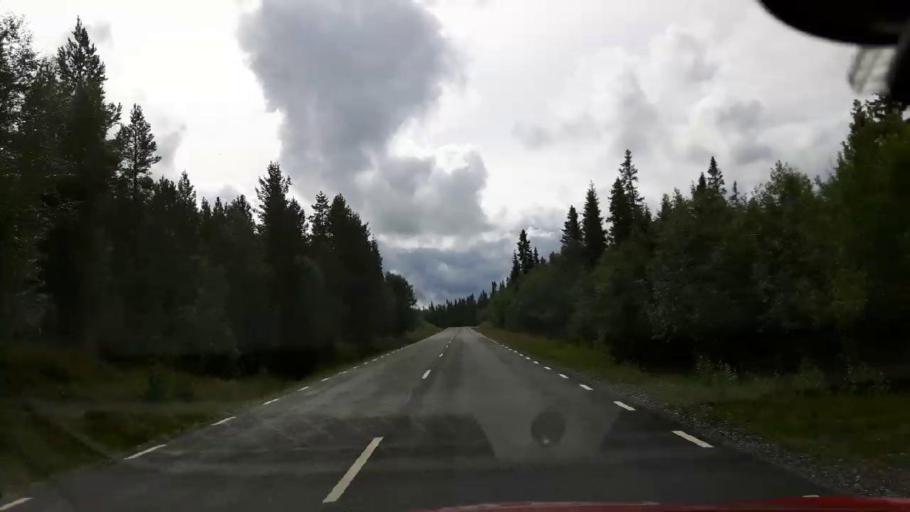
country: NO
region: Nord-Trondelag
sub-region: Lierne
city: Sandvika
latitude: 64.6139
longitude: 14.1208
